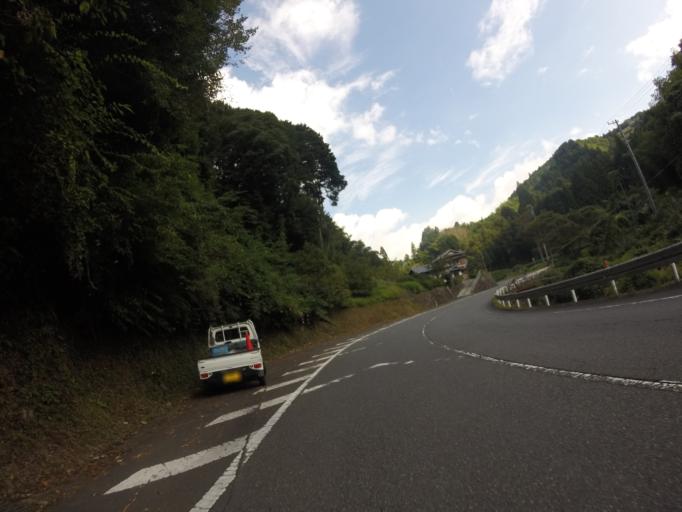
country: JP
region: Shizuoka
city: Shizuoka-shi
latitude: 35.0987
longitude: 138.4650
